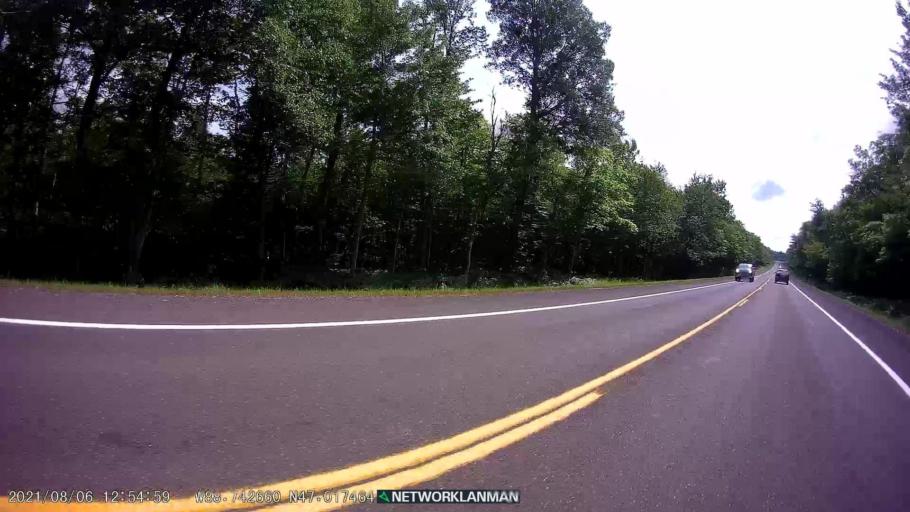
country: US
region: Michigan
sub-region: Houghton County
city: Hancock
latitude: 47.0170
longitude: -88.7434
